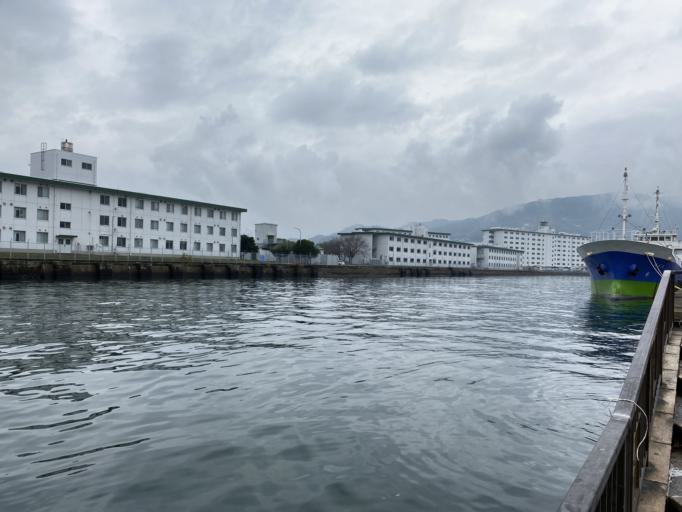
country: JP
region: Nagasaki
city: Sasebo
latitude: 33.1629
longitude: 129.7213
